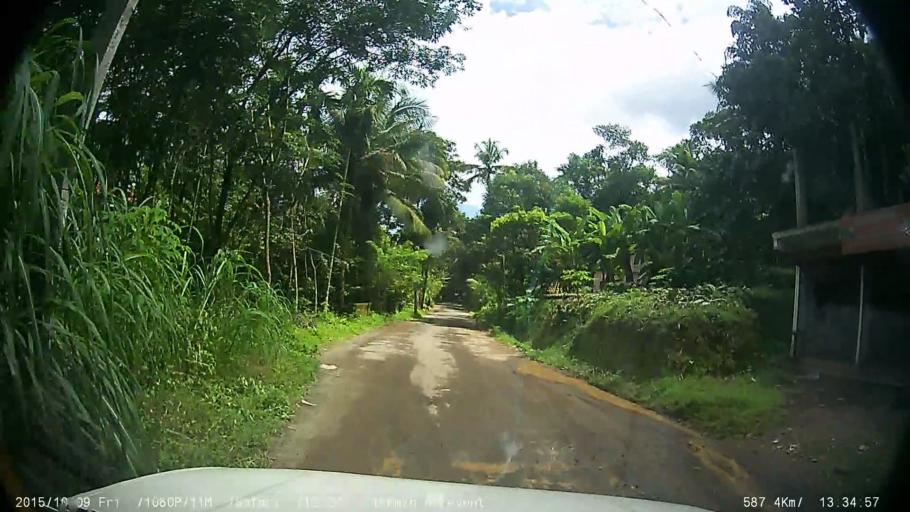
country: IN
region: Kerala
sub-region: Ernakulam
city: Ramamangalam
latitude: 9.9035
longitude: 76.5578
